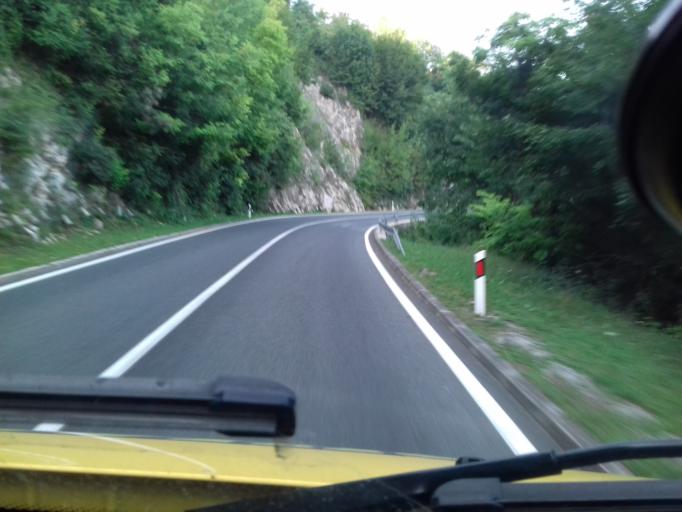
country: BA
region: Federation of Bosnia and Herzegovina
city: Ostrozac
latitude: 44.9022
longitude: 15.9306
